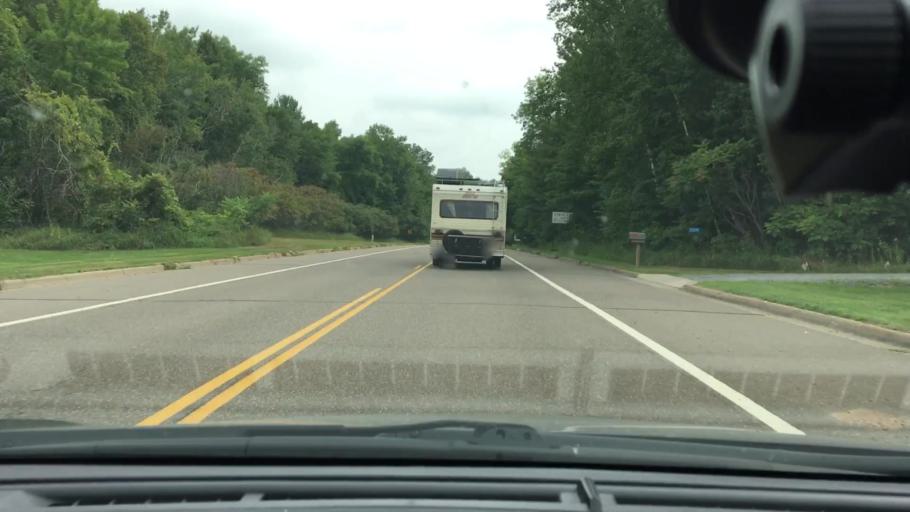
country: US
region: Minnesota
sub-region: Crow Wing County
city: Crosby
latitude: 46.4097
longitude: -93.8675
